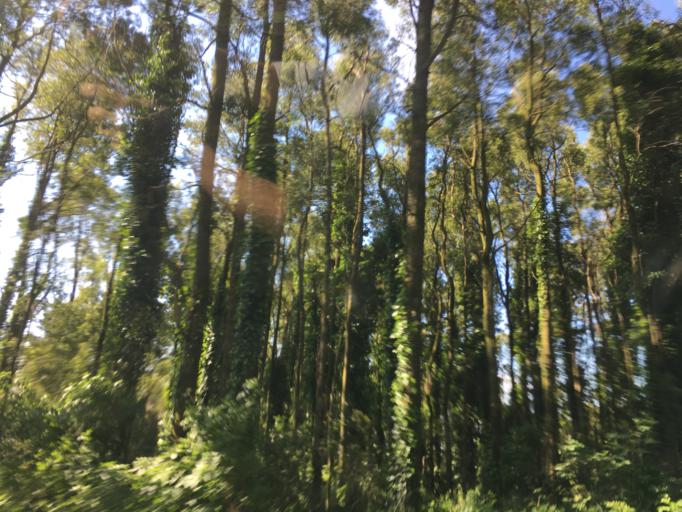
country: PT
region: Lisbon
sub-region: Sintra
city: Colares
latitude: 38.7712
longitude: -9.4521
